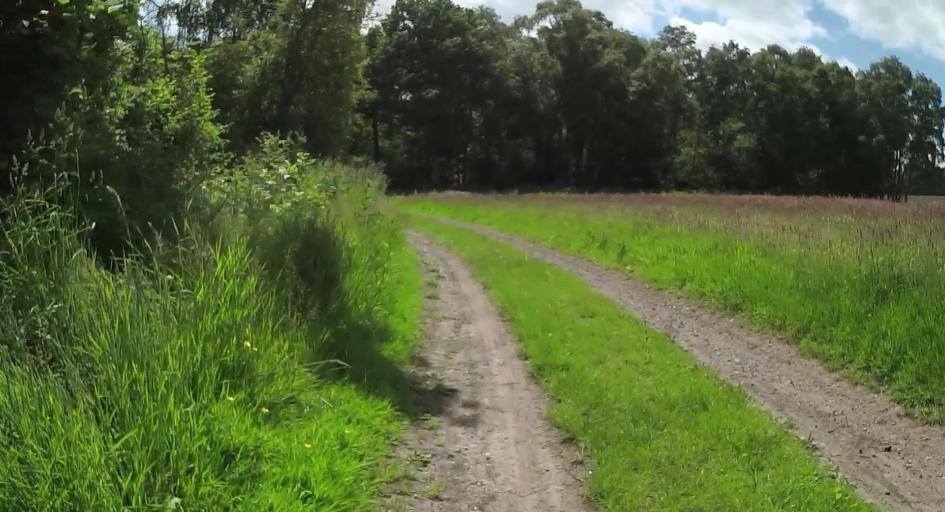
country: GB
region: England
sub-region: Hampshire
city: Basingstoke
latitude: 51.1926
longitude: -1.1656
